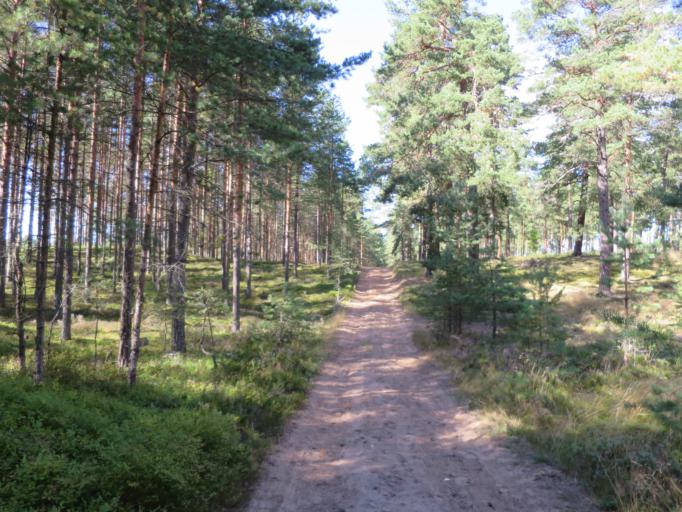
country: LV
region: Riga
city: Jaunciems
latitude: 57.0638
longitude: 24.2264
